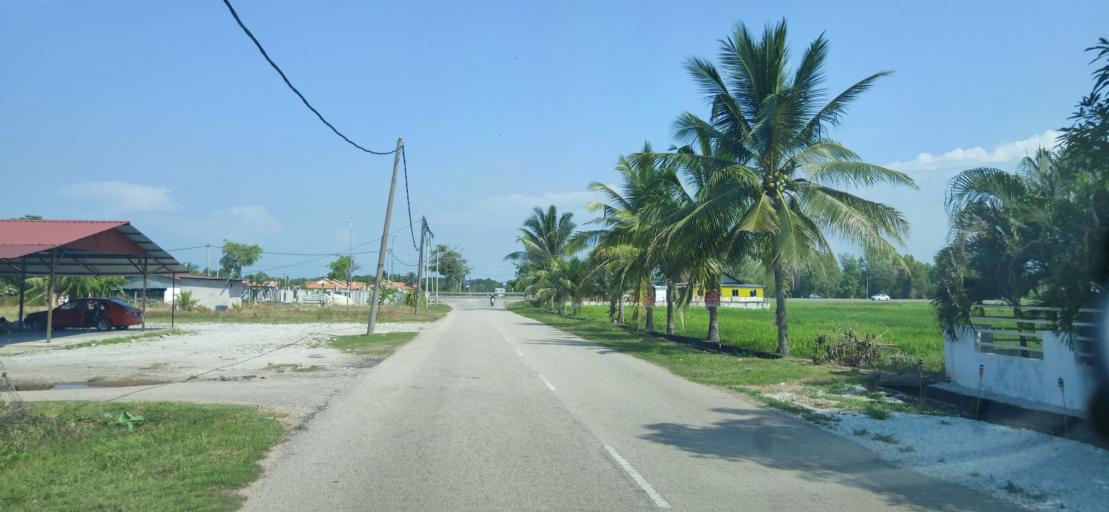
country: MY
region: Kedah
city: Sungai Petani
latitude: 5.6603
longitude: 100.4666
